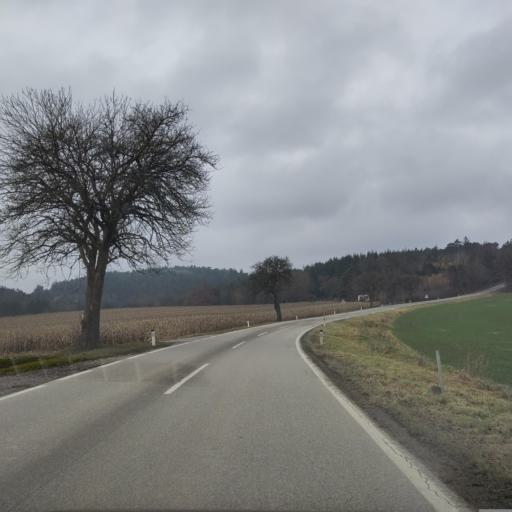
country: AT
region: Lower Austria
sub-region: Politischer Bezirk Sankt Polten
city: Karlstetten
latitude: 48.2637
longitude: 15.5494
